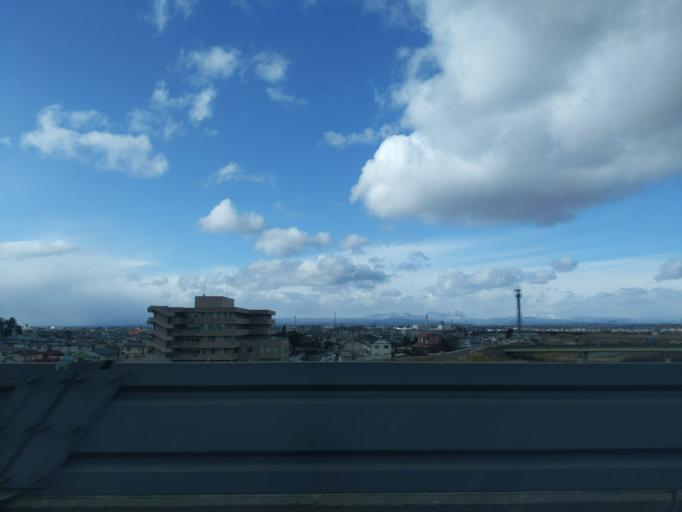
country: JP
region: Miyagi
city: Furukawa
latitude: 38.5884
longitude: 140.9741
